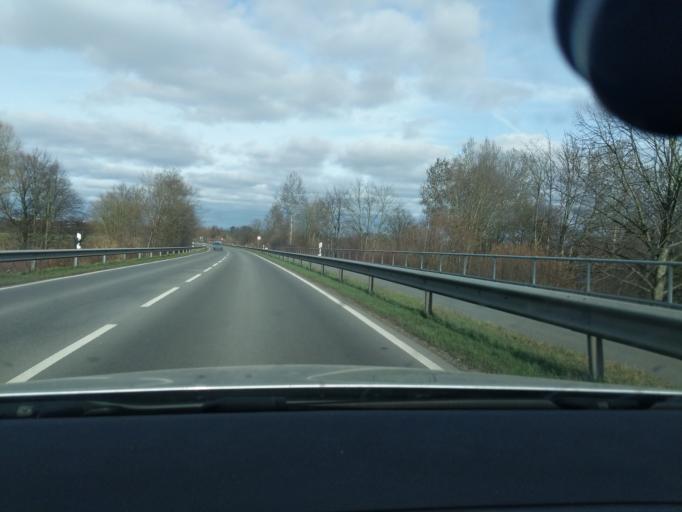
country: DE
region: Lower Saxony
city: Agathenburg
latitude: 53.5729
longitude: 9.5196
